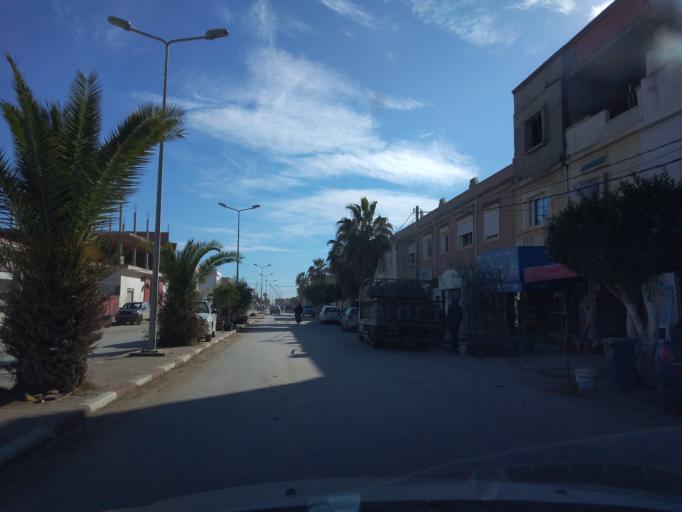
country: TN
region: Ariana
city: Qal'at al Andalus
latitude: 37.0603
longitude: 10.1191
